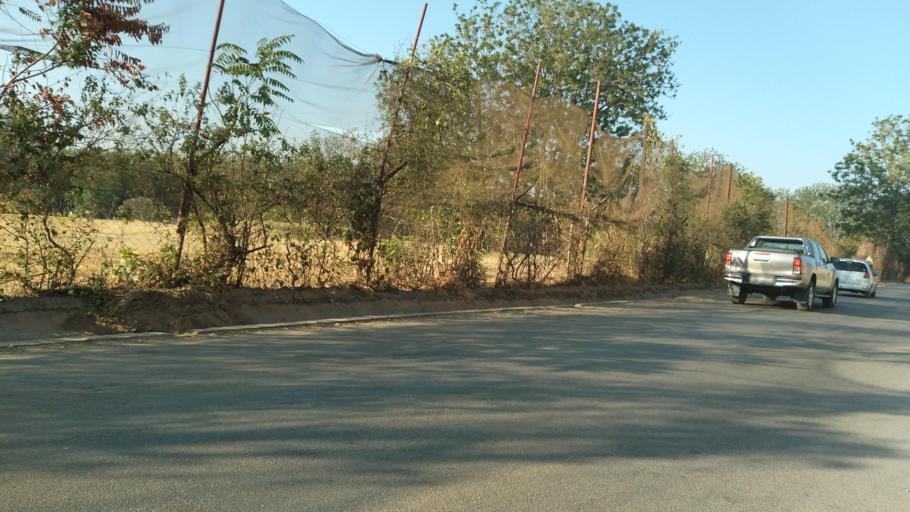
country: ZM
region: Lusaka
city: Lusaka
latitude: -15.5488
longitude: 28.2717
